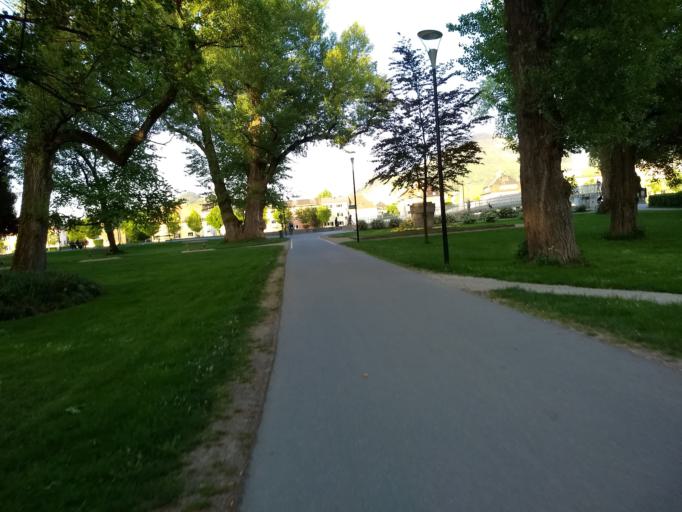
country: AT
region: Salzburg
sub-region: Salzburg Stadt
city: Salzburg
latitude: 47.8146
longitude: 13.0349
